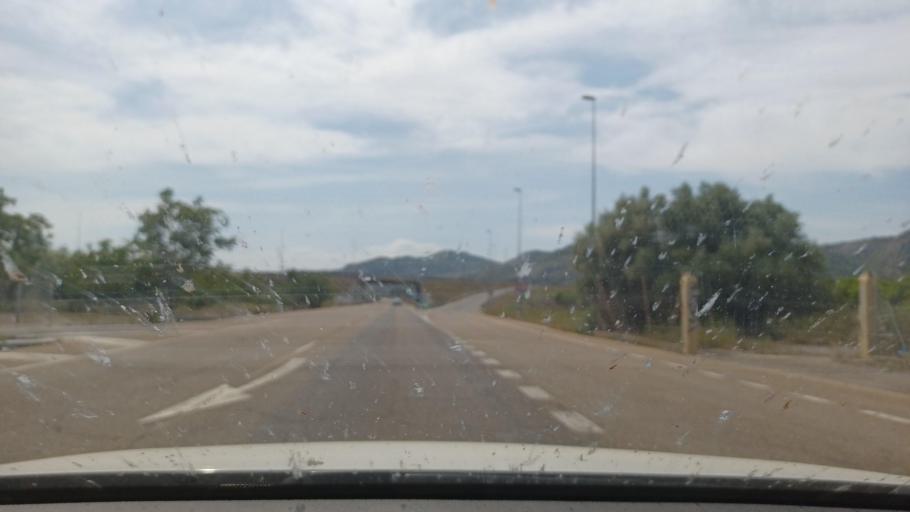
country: ES
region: Valencia
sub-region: Provincia de Castello
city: Castello de la Plana
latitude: 40.0251
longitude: -0.0155
